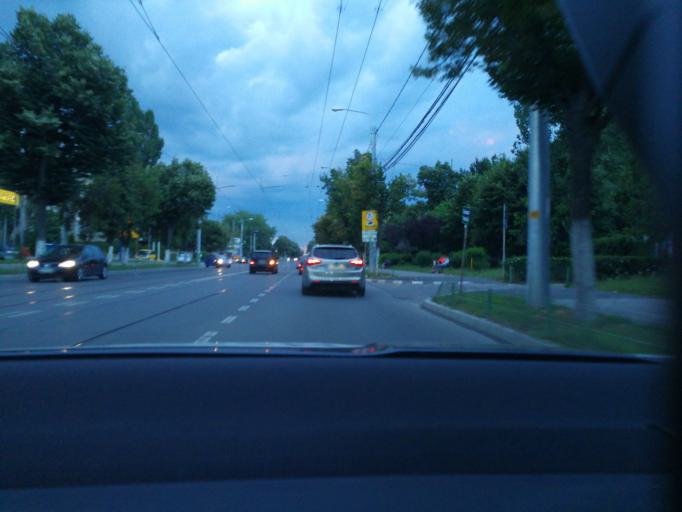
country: RO
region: Prahova
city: Ploiesti
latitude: 44.9404
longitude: 25.9910
